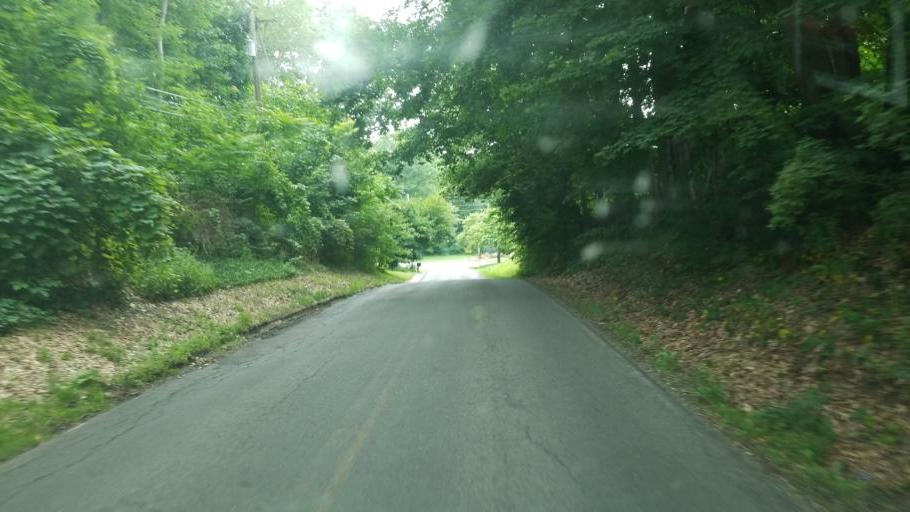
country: US
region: Ohio
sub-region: Summit County
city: Clinton
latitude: 40.9293
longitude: -81.6245
